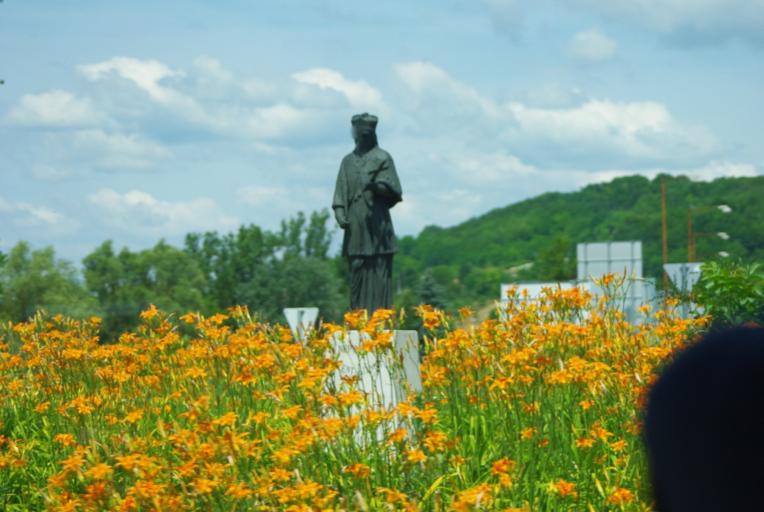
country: HU
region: Nograd
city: Balassagyarmat
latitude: 48.0858
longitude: 19.2994
